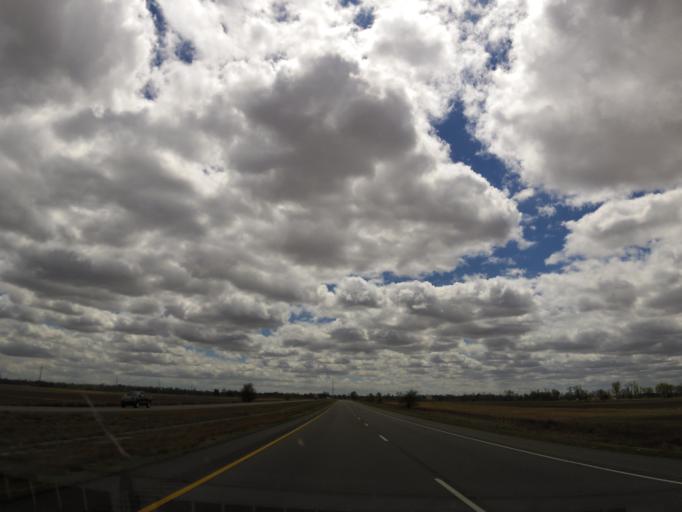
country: US
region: Arkansas
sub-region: Poinsett County
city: Marked Tree
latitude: 35.5628
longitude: -90.4971
